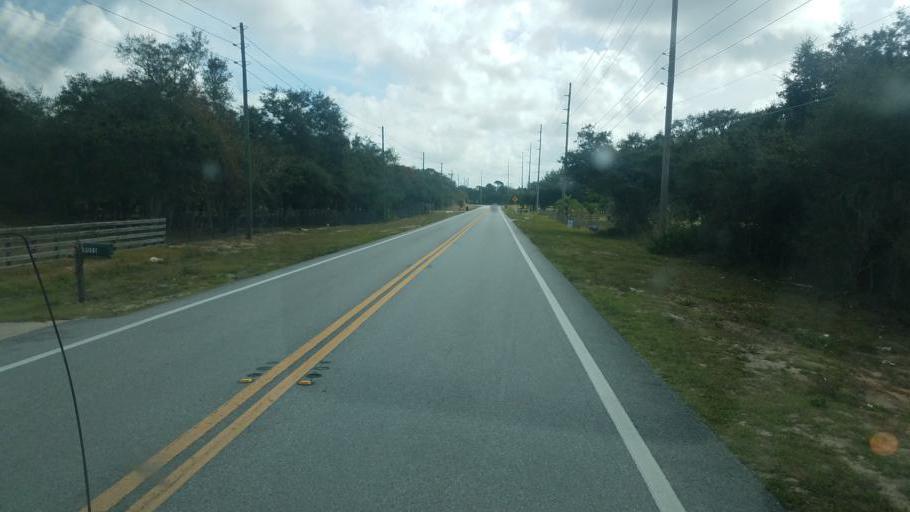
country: US
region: Florida
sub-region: Polk County
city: Dundee
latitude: 28.0293
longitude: -81.5180
